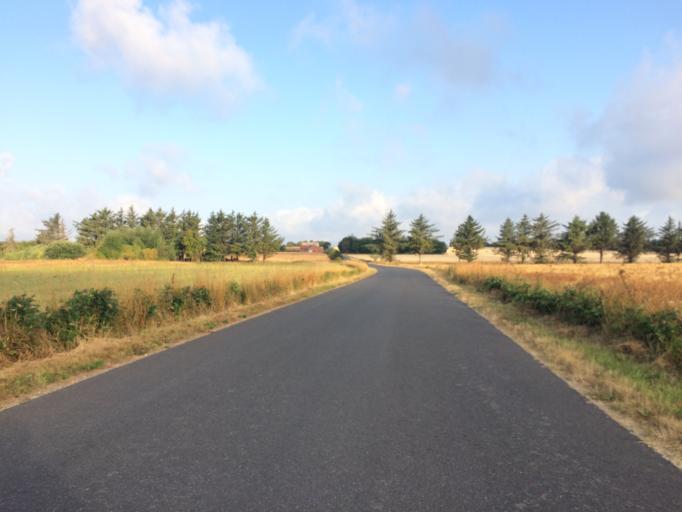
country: DK
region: Central Jutland
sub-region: Holstebro Kommune
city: Vinderup
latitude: 56.6032
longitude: 8.7170
